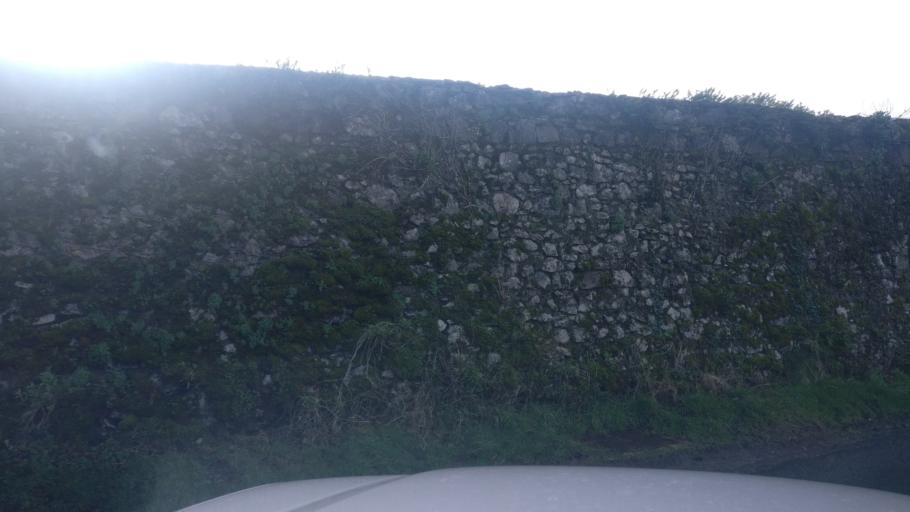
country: IE
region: Connaught
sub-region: County Galway
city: Loughrea
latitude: 53.2838
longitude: -8.5945
